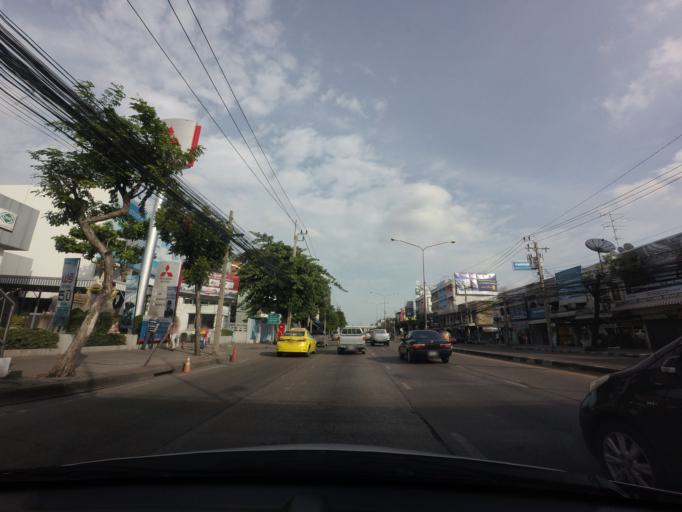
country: TH
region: Bangkok
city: Bueng Kum
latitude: 13.7969
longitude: 100.6506
